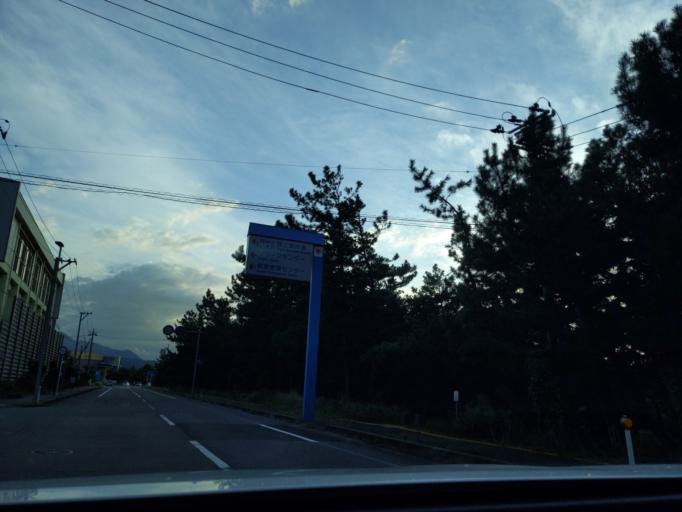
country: JP
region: Niigata
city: Kashiwazaki
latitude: 37.3756
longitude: 138.5541
